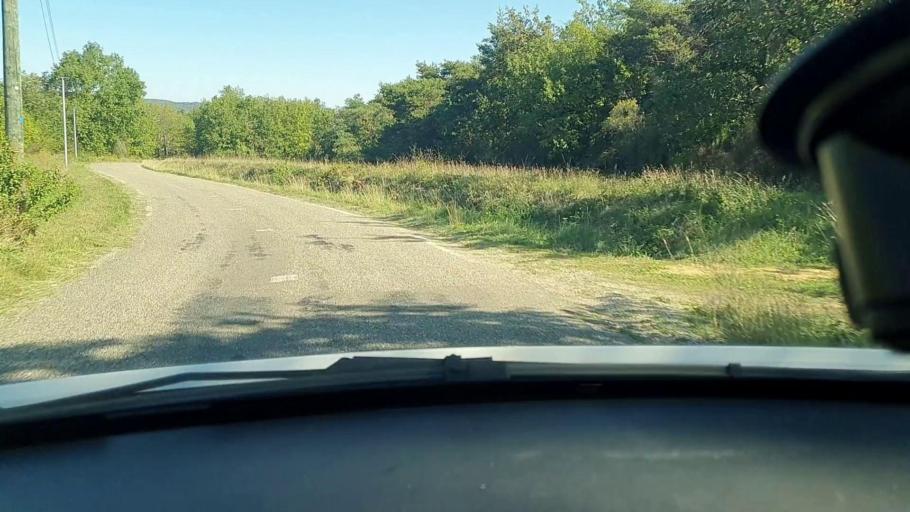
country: FR
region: Languedoc-Roussillon
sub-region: Departement du Gard
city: Saint-Julien-de-Peyrolas
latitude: 44.2732
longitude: 4.5353
